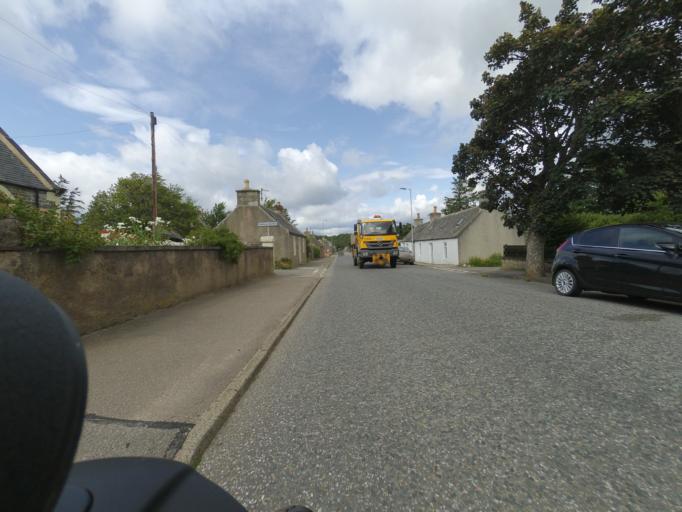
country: GB
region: Scotland
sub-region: Highland
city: Grantown on Spey
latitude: 57.2534
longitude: -3.3816
